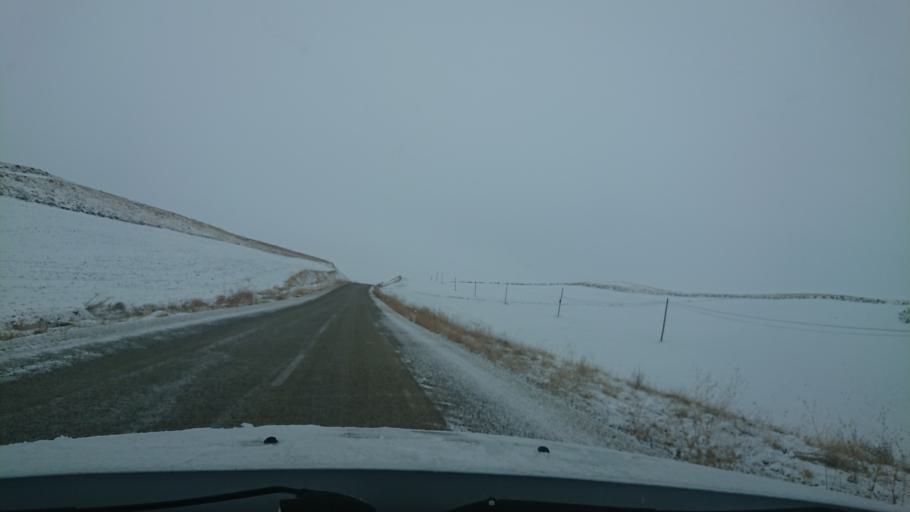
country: TR
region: Aksaray
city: Agacoren
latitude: 38.7889
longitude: 33.8711
